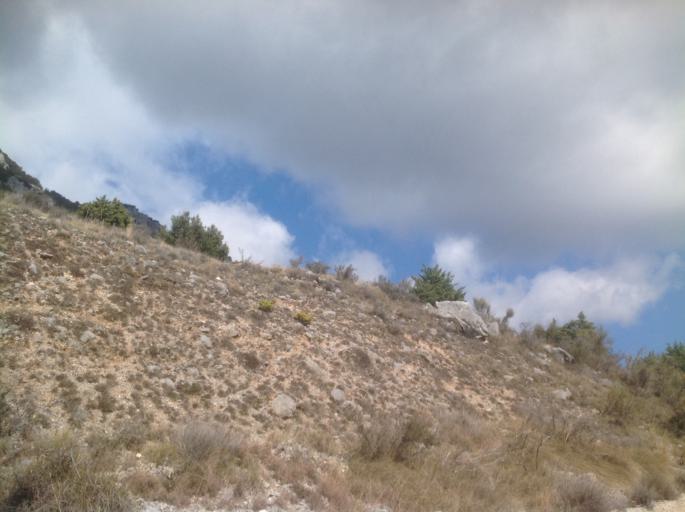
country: IT
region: Calabria
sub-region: Provincia di Cosenza
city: Civita
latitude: 39.8358
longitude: 16.3019
